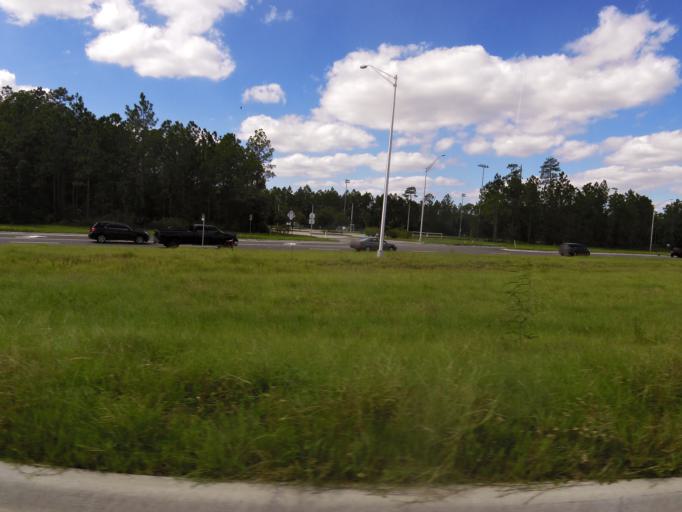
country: US
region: Florida
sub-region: Saint Johns County
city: Fruit Cove
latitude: 30.0784
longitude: -81.5314
